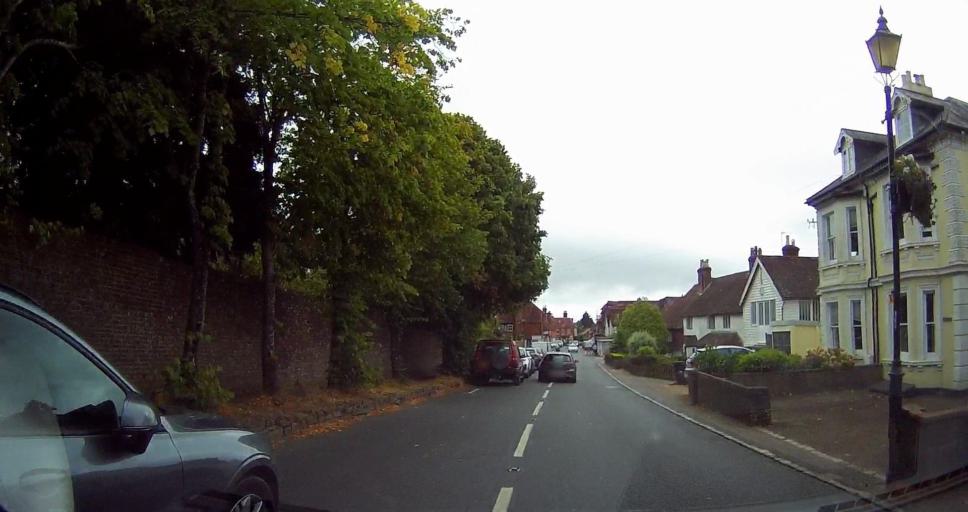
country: GB
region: England
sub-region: East Sussex
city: Wadhurst
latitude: 51.0633
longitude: 0.3372
